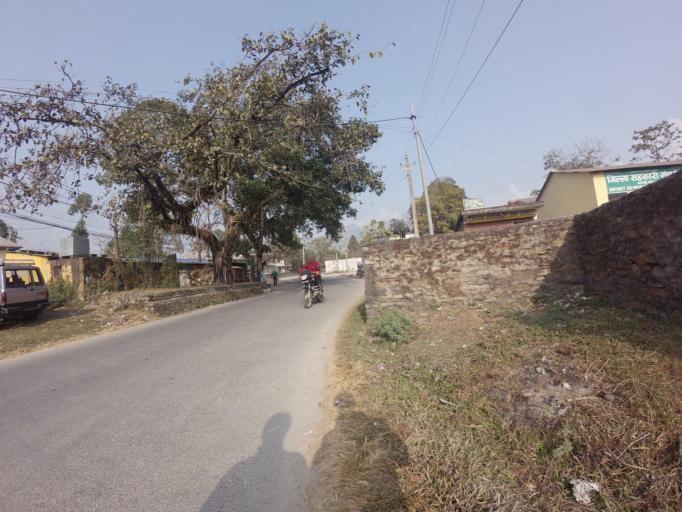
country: NP
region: Western Region
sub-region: Gandaki Zone
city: Pokhara
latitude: 28.2028
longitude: 83.9695
